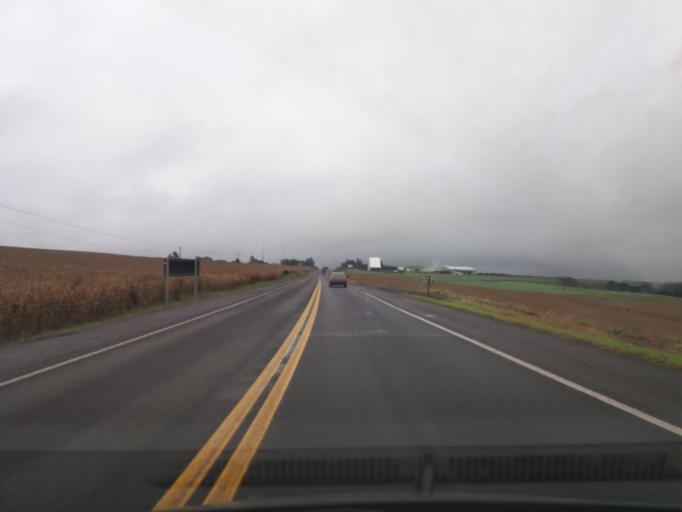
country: BR
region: Parana
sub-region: Ampere
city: Ampere
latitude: -25.9117
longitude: -53.4324
